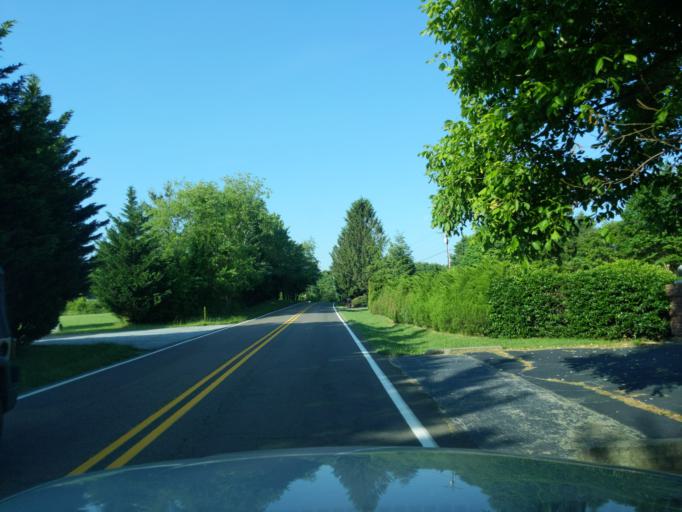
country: US
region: North Carolina
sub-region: Henderson County
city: Hoopers Creek
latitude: 35.4601
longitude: -82.4688
